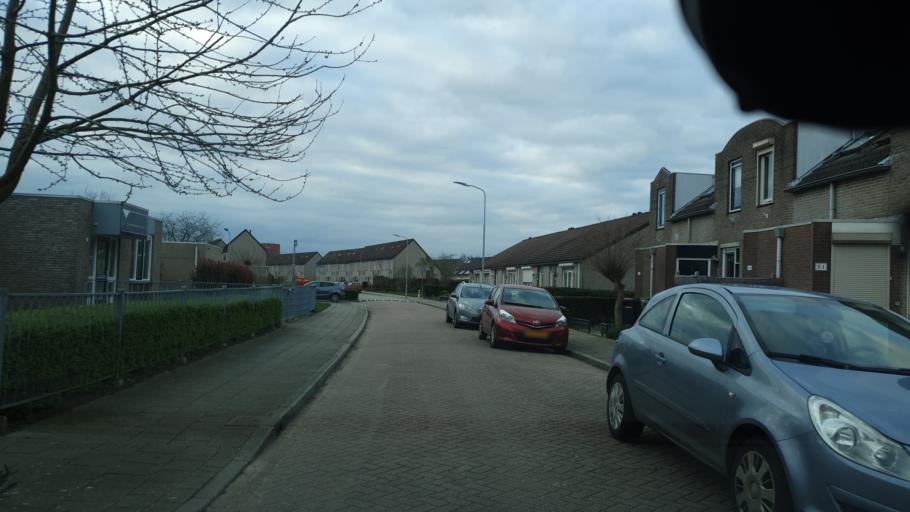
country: NL
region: Gelderland
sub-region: Gemeente Duiven
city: Duiven
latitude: 51.9520
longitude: 6.0323
